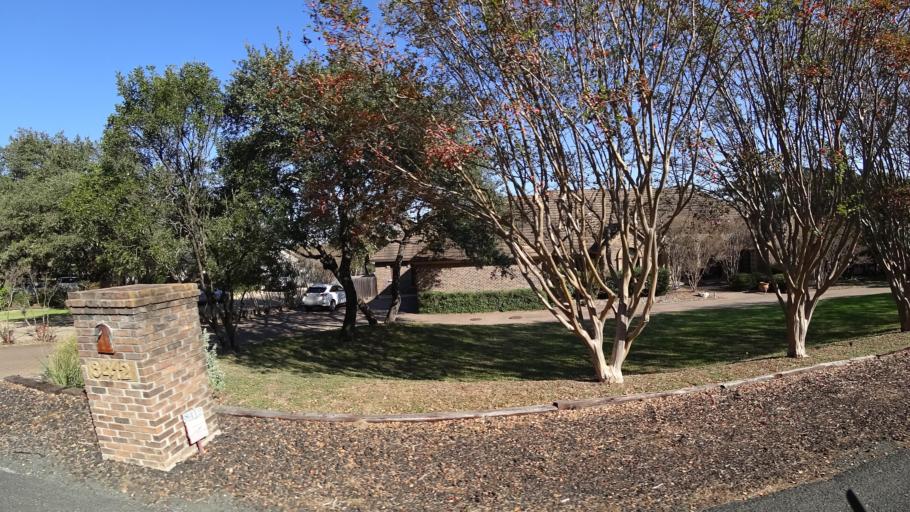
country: US
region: Texas
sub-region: Williamson County
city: Jollyville
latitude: 30.3767
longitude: -97.8159
